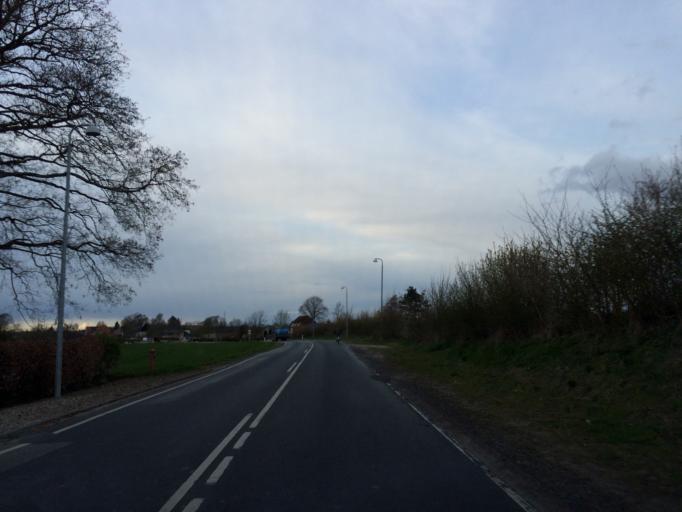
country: DK
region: South Denmark
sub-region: Odense Kommune
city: Bellinge
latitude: 55.3569
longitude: 10.2771
